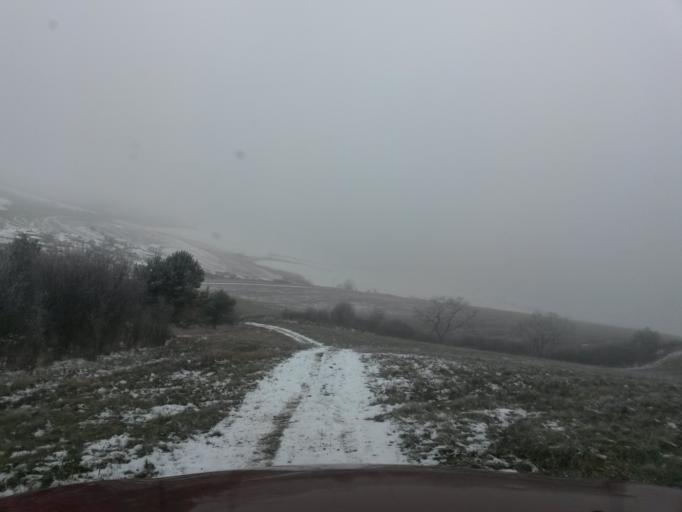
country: SK
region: Kosicky
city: Krompachy
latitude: 48.9689
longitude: 20.9771
